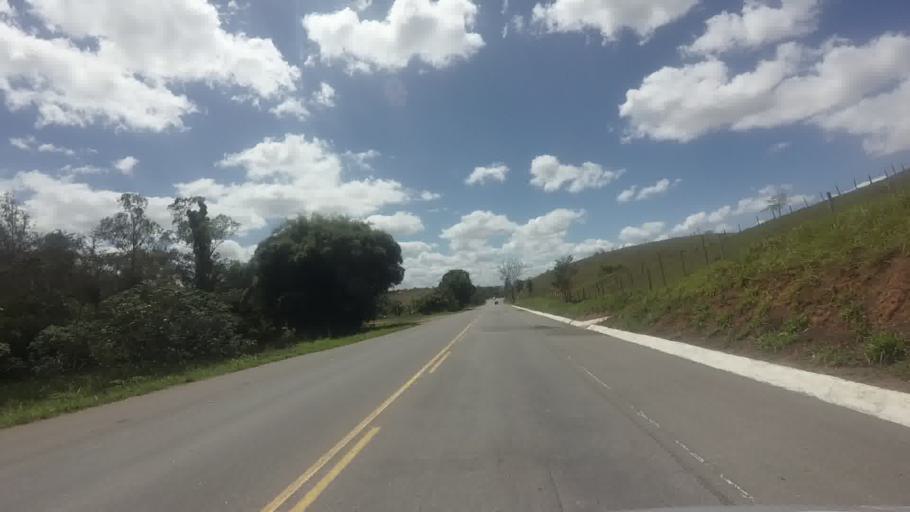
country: BR
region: Minas Gerais
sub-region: Recreio
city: Recreio
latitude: -21.6560
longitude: -42.3690
